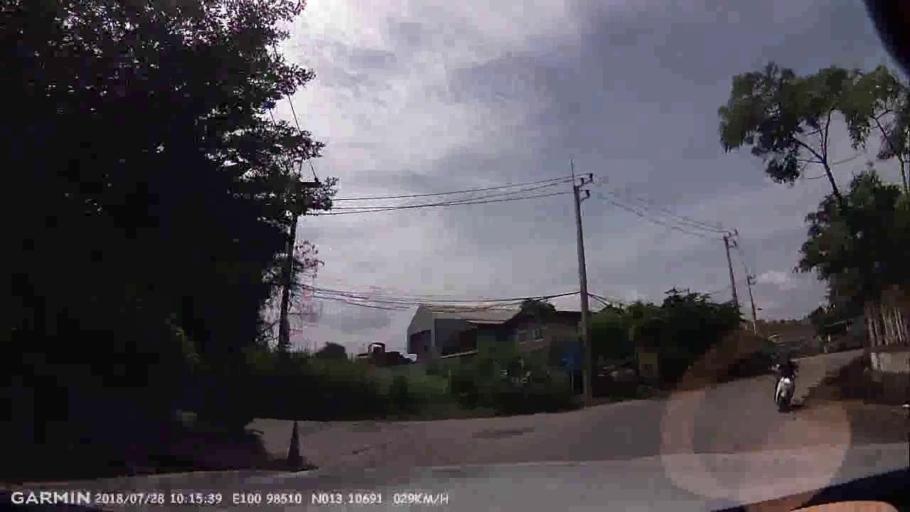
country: TH
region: Chon Buri
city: Ban Talat Bueng
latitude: 13.1069
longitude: 100.9852
